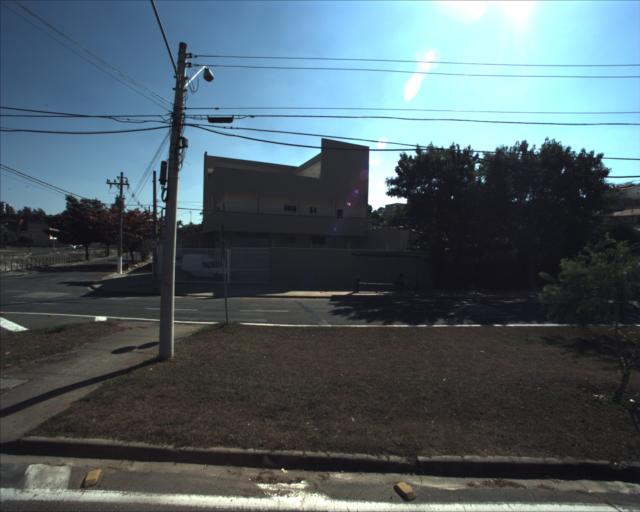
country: BR
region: Sao Paulo
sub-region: Sorocaba
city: Sorocaba
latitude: -23.5070
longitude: -47.4334
